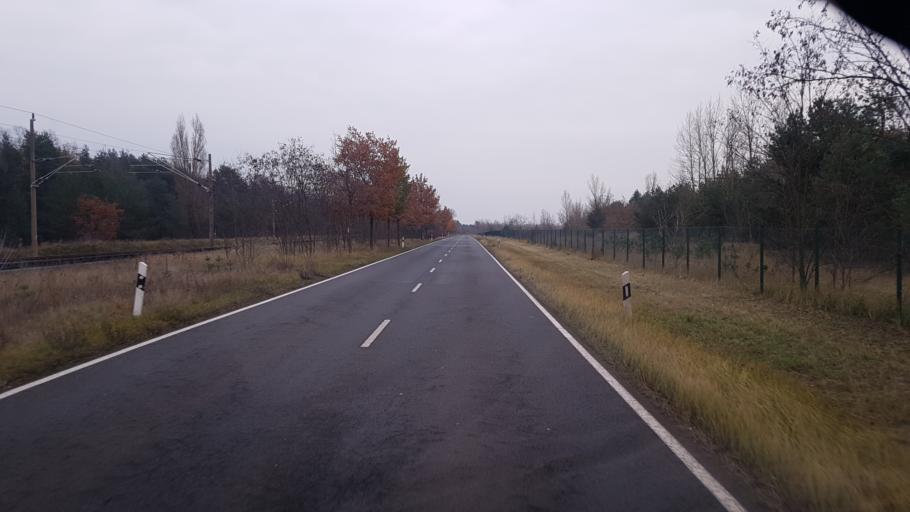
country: DE
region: Brandenburg
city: Eisenhuettenstadt
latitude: 52.1642
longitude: 14.6514
